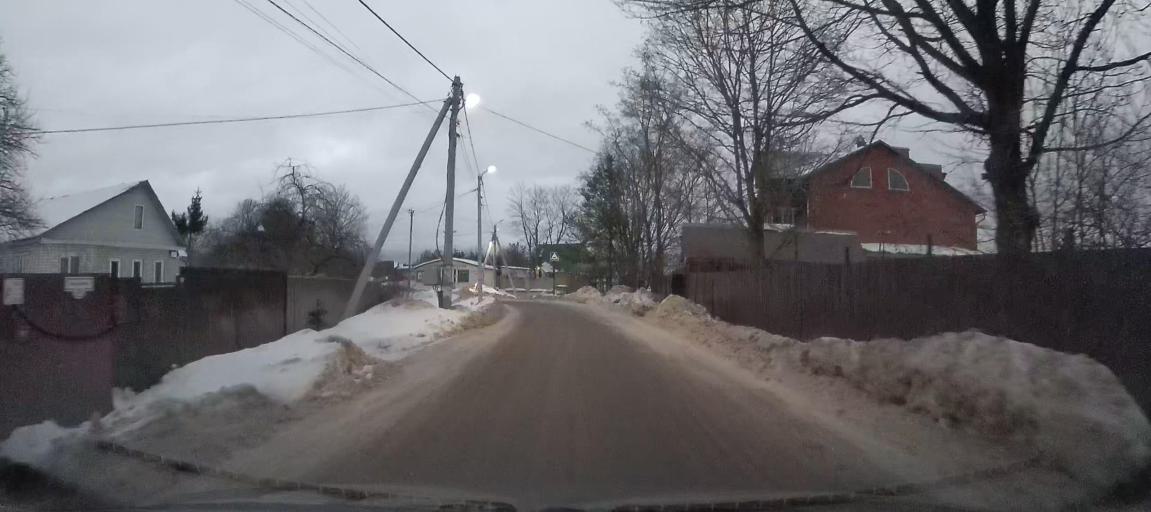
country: RU
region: Leningrad
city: Taytsy
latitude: 59.6974
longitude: 30.1395
